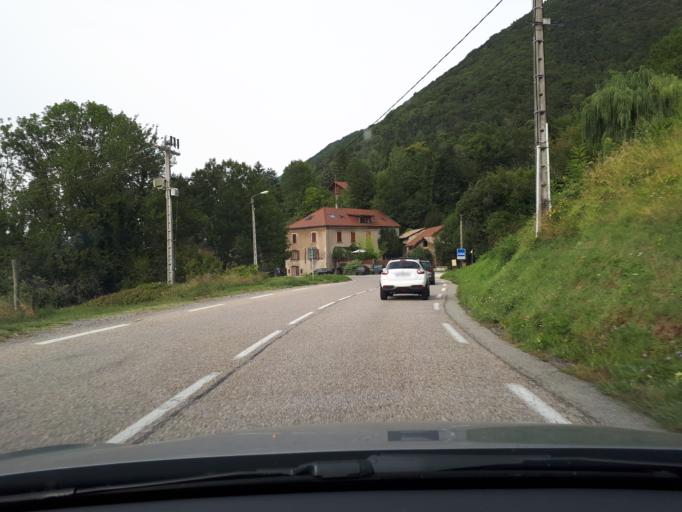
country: FR
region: Rhone-Alpes
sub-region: Departement de l'Isere
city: Saint-Georges-de-Commiers
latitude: 45.0146
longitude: 5.7038
